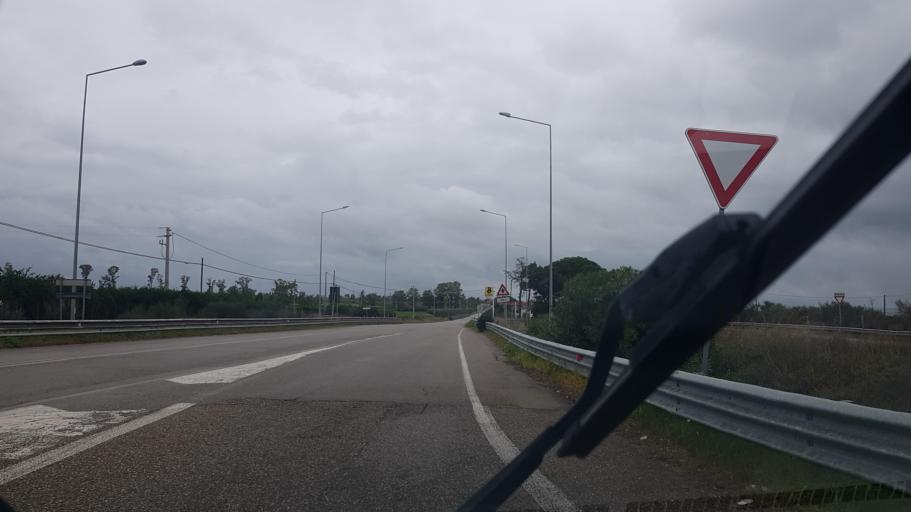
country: IT
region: Apulia
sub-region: Provincia di Taranto
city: Marina di Ginosa
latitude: 40.4038
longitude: 16.8059
